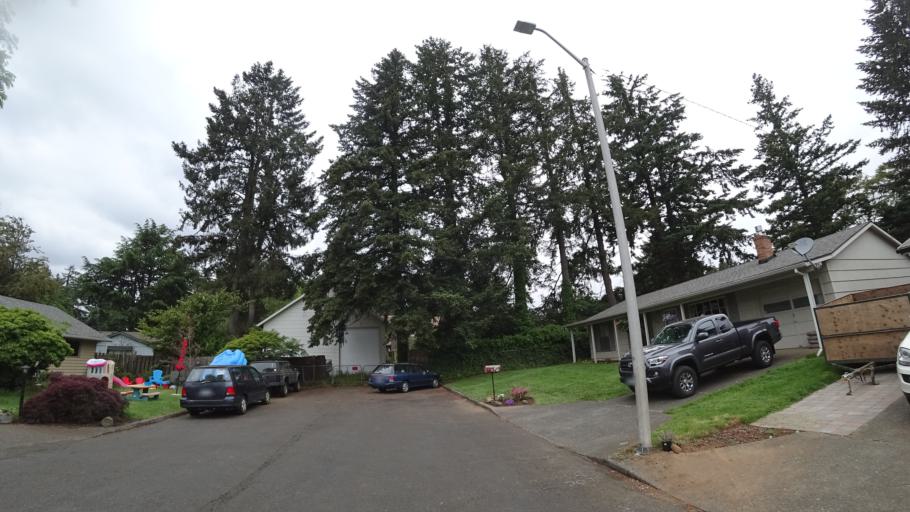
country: US
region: Oregon
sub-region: Multnomah County
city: Lents
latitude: 45.5075
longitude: -122.5237
